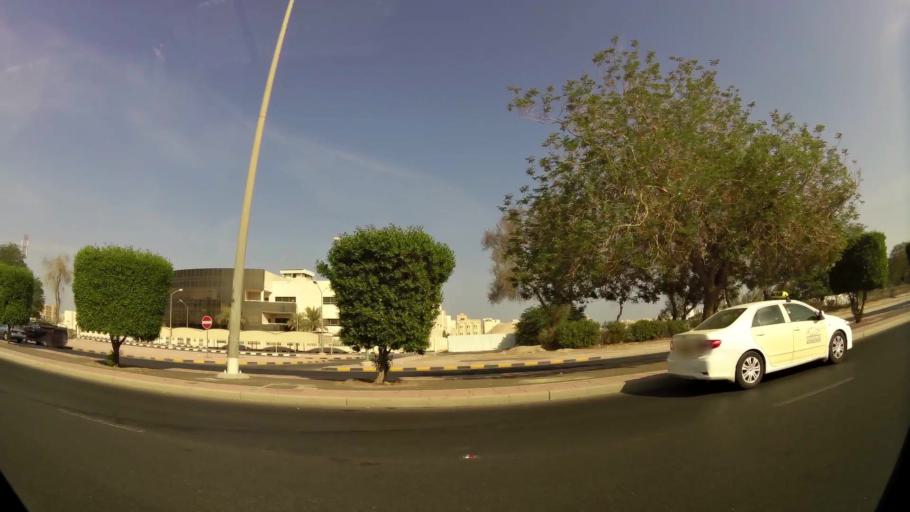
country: KW
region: Al Ahmadi
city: Ar Riqqah
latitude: 29.1622
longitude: 48.1023
